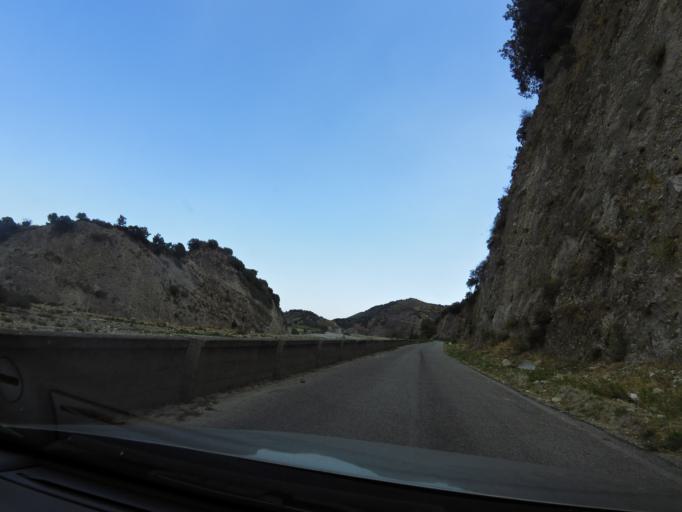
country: IT
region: Calabria
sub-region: Provincia di Reggio Calabria
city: Stilo
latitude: 38.4647
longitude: 16.4919
